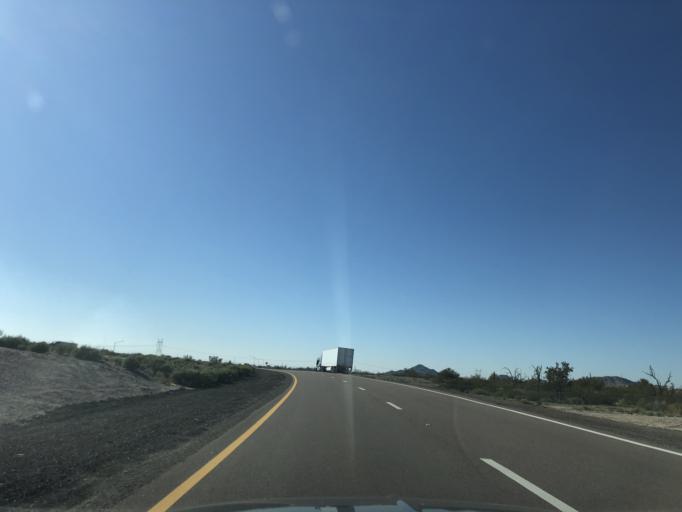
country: US
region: Arizona
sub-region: Maricopa County
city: Buckeye
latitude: 33.4453
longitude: -112.5572
